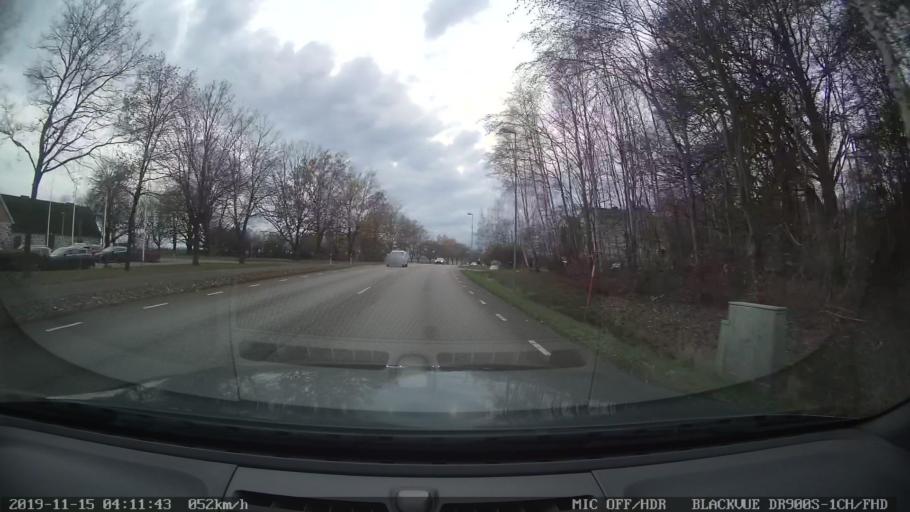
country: SE
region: Skane
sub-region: Helsingborg
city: Odakra
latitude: 56.0862
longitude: 12.7415
